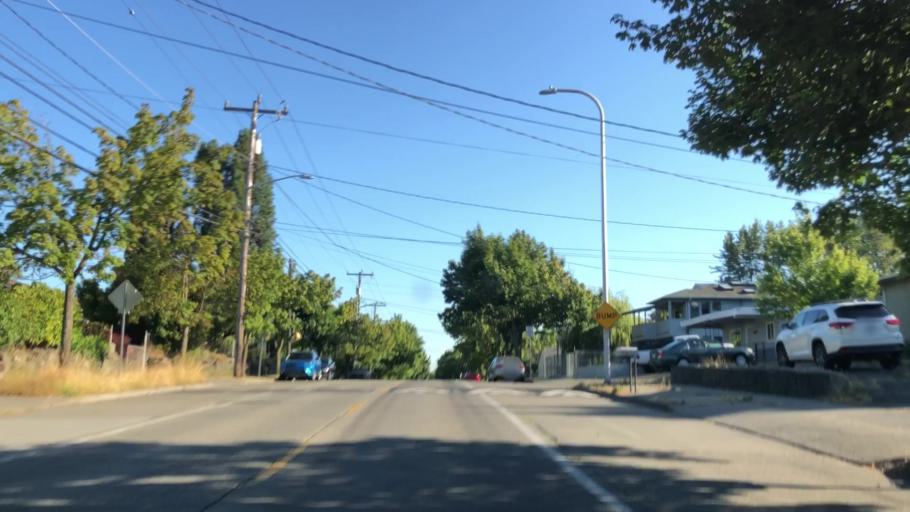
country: US
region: Washington
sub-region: King County
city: White Center
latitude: 47.5396
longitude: -122.3551
